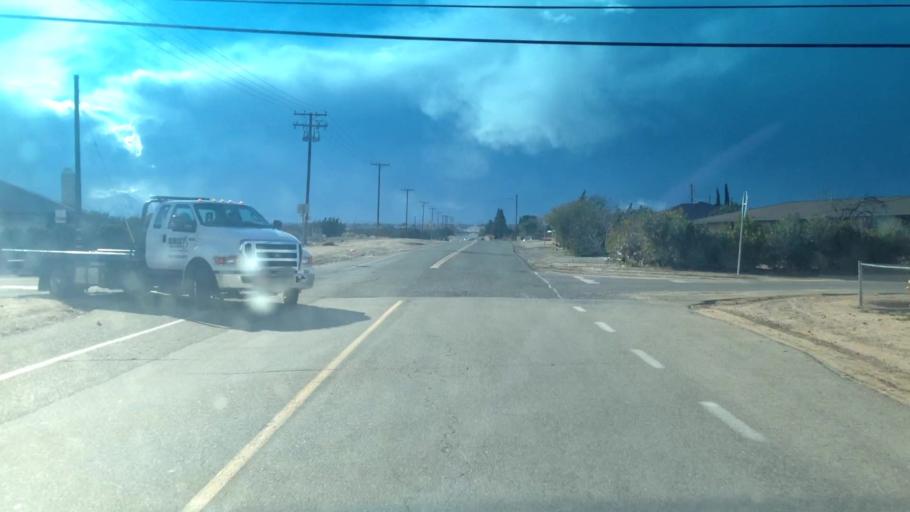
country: US
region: California
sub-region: San Bernardino County
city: Hesperia
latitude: 34.3837
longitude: -117.2844
